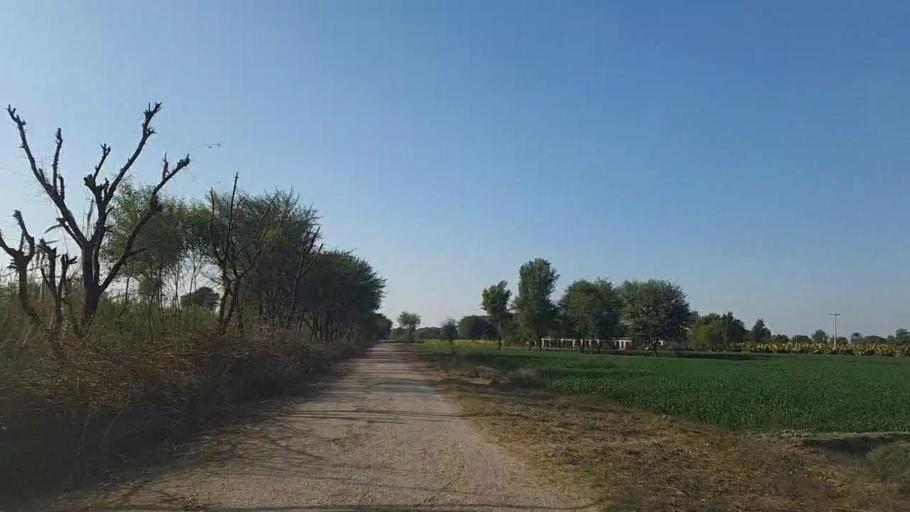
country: PK
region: Sindh
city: Shahpur Chakar
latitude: 26.1939
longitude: 68.6349
